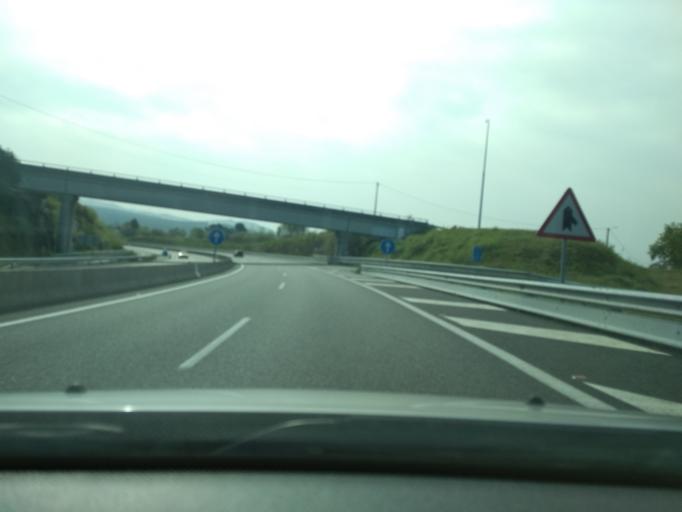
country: ES
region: Galicia
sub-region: Provincia da Coruna
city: Rianxo
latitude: 42.6701
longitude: -8.8278
